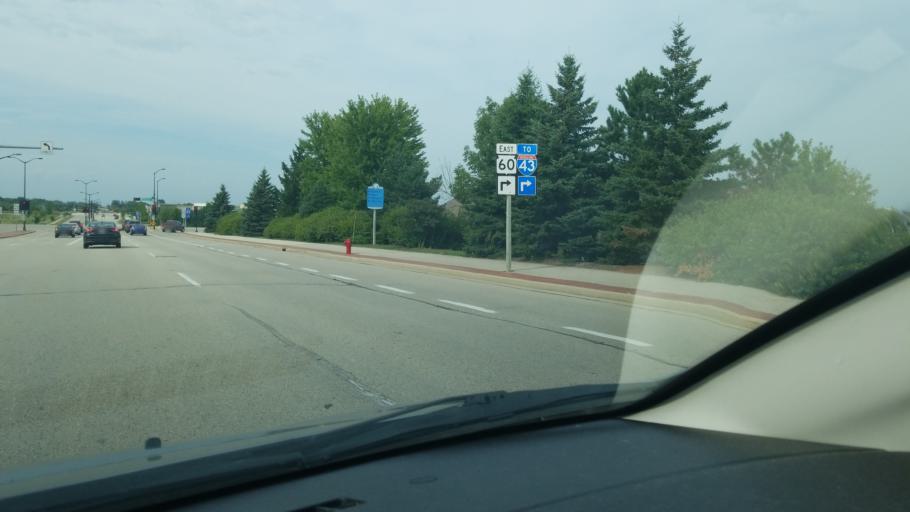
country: US
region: Wisconsin
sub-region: Ozaukee County
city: Grafton
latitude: 43.3190
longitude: -87.9252
